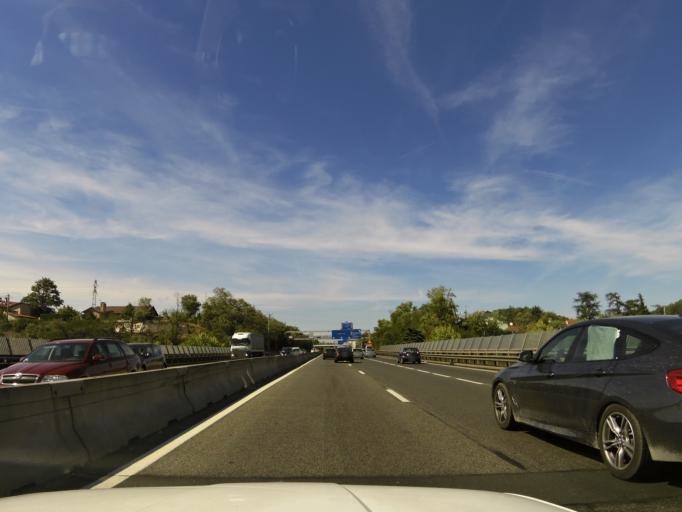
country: FR
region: Rhone-Alpes
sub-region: Departement de l'Isere
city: Chasse-sur-Rhone
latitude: 45.5797
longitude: 4.8027
